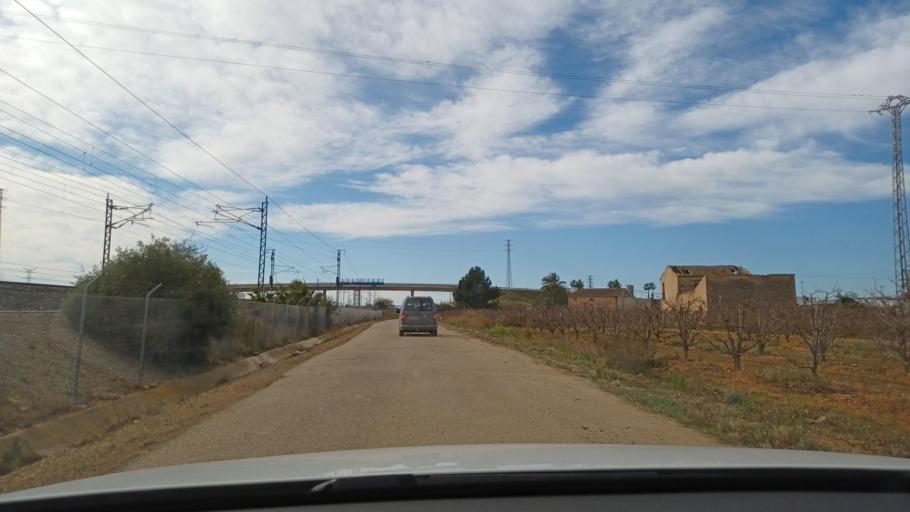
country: ES
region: Valencia
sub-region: Provincia de Valencia
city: Benifaio
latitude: 39.2905
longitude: -0.4383
